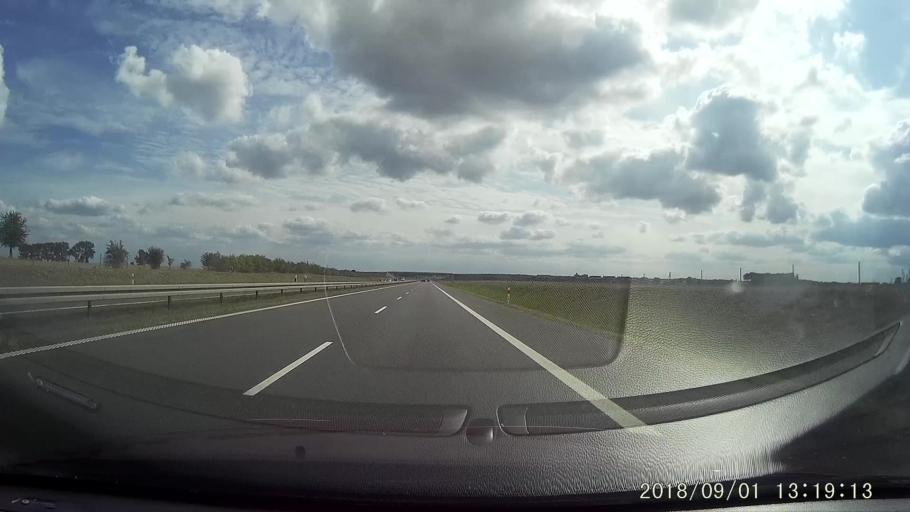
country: PL
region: West Pomeranian Voivodeship
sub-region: Powiat pyrzycki
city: Bielice
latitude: 53.1969
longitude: 14.6844
